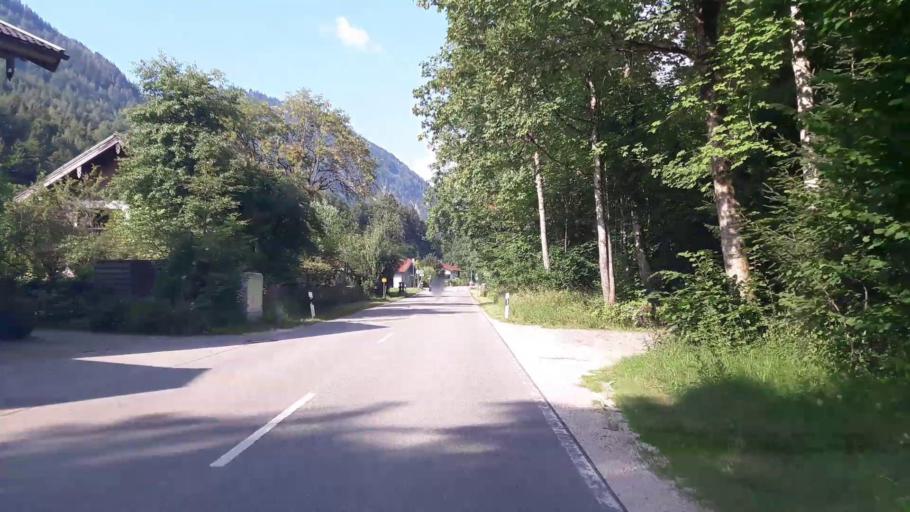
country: DE
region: Bavaria
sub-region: Upper Bavaria
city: Ruhpolding
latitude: 47.7429
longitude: 12.6160
